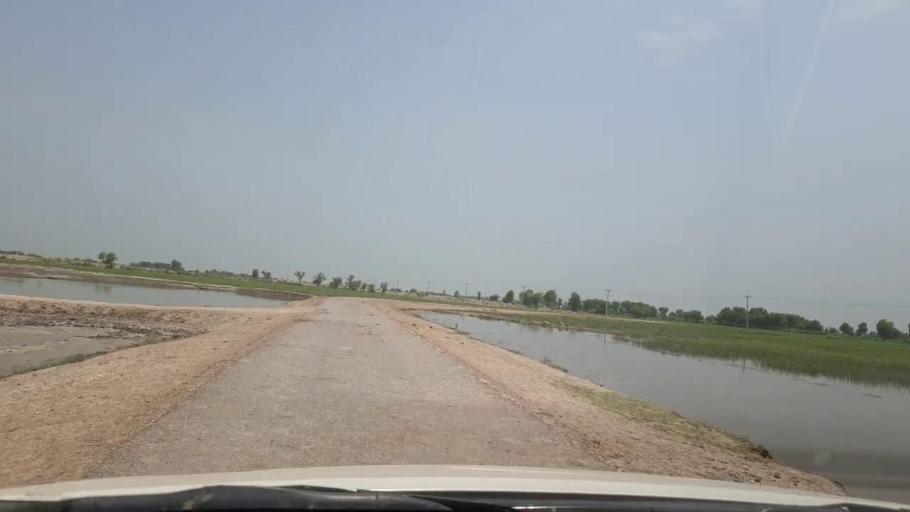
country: PK
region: Sindh
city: Rustam jo Goth
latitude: 28.0186
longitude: 68.7836
